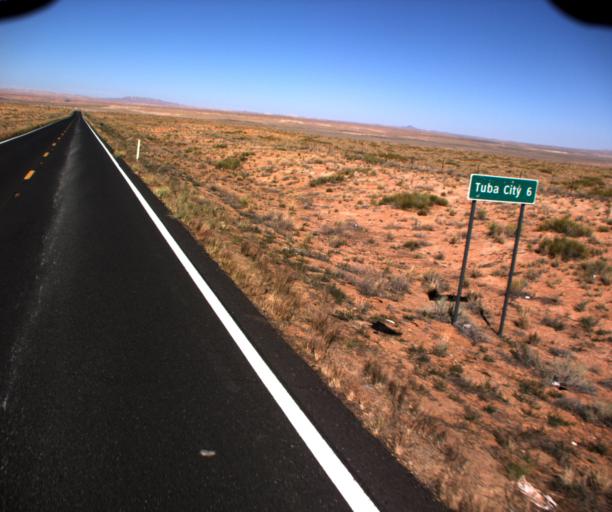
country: US
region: Arizona
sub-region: Coconino County
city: Tuba City
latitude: 36.0693
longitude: -111.1840
